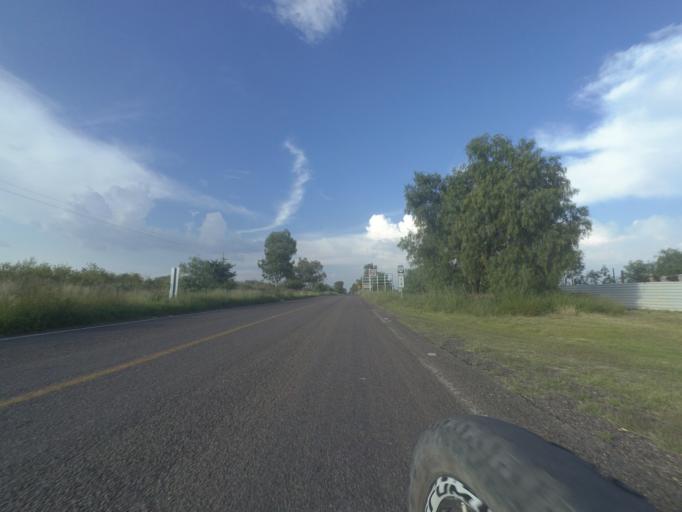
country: MX
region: Aguascalientes
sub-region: Aguascalientes
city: Penuelas (El Cienegal)
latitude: 21.7228
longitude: -102.3637
